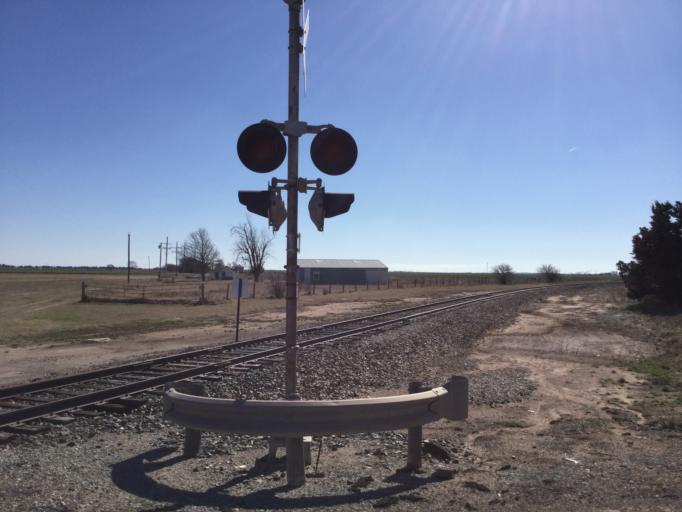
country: US
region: Kansas
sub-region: Barber County
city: Kiowa
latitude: 37.0064
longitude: -98.4899
